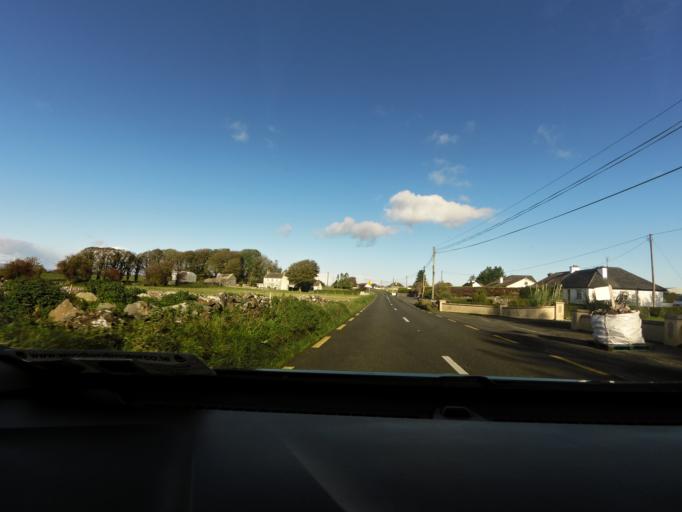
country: IE
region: Connaught
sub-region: Maigh Eo
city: Ballinrobe
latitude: 53.5585
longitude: -9.1083
